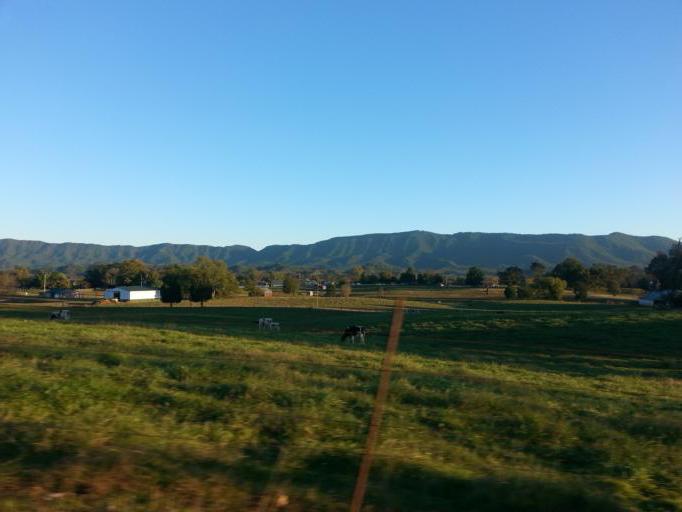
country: US
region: Tennessee
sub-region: Blount County
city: Wildwood
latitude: 35.8188
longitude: -83.7856
